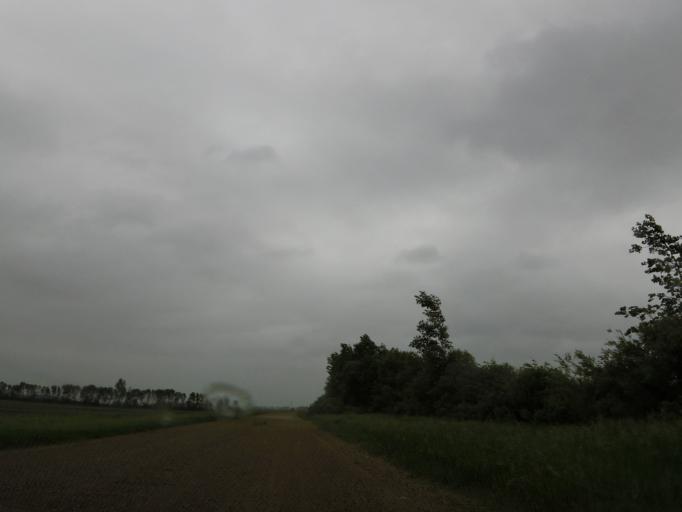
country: US
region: North Dakota
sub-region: Walsh County
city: Grafton
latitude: 48.4354
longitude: -97.4055
